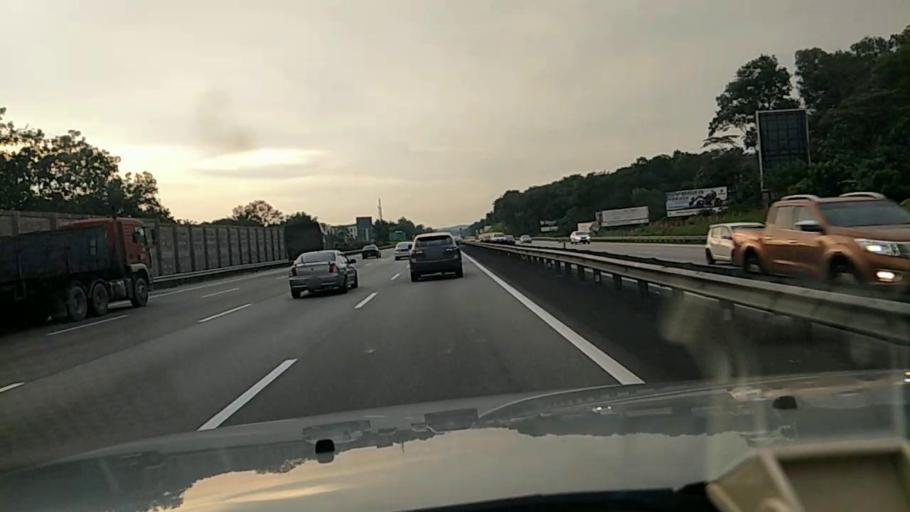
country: MY
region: Selangor
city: Kuang
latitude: 3.2499
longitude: 101.5641
